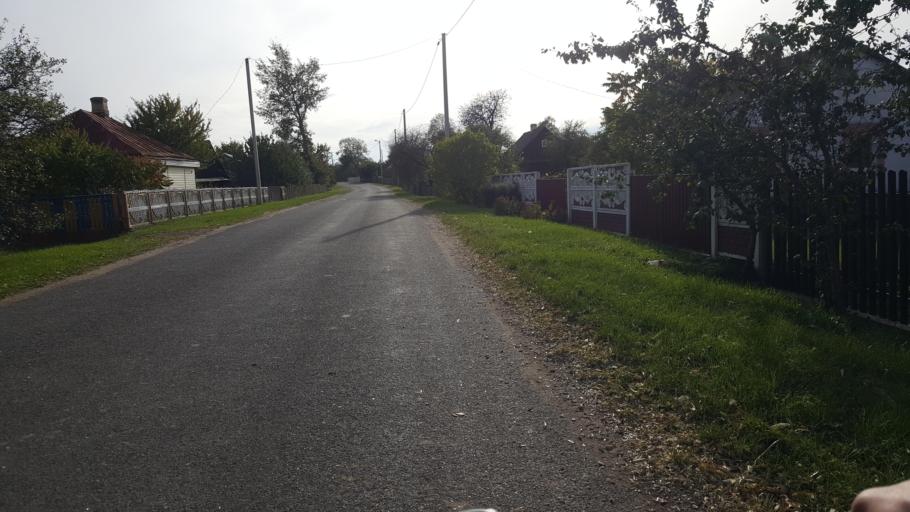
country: BY
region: Brest
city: Kamyanyets
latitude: 52.4061
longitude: 23.8878
